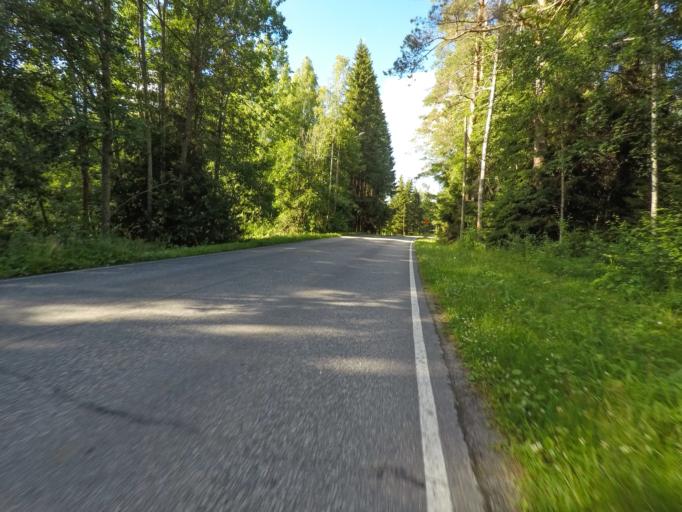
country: FI
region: South Karelia
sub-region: Imatra
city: Imatra
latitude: 61.1497
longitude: 28.7534
